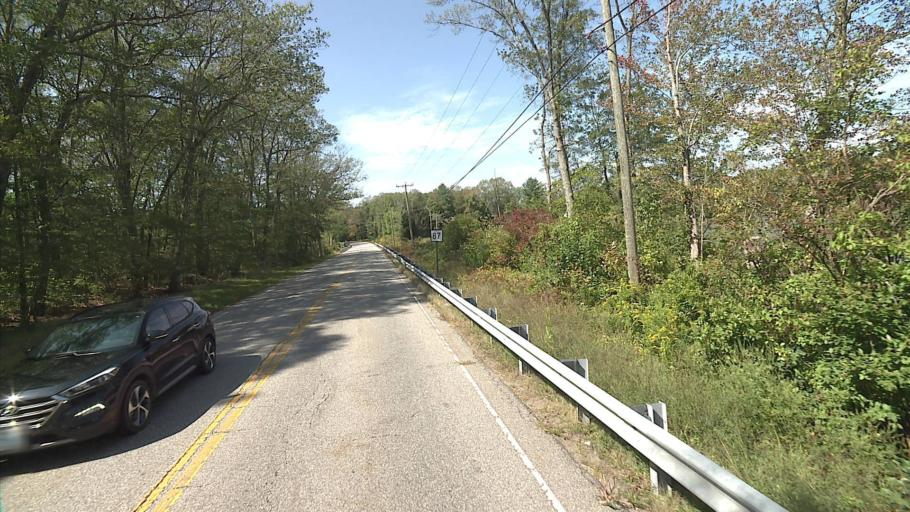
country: US
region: Connecticut
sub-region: Windham County
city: Willimantic
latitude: 41.6682
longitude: -72.2577
